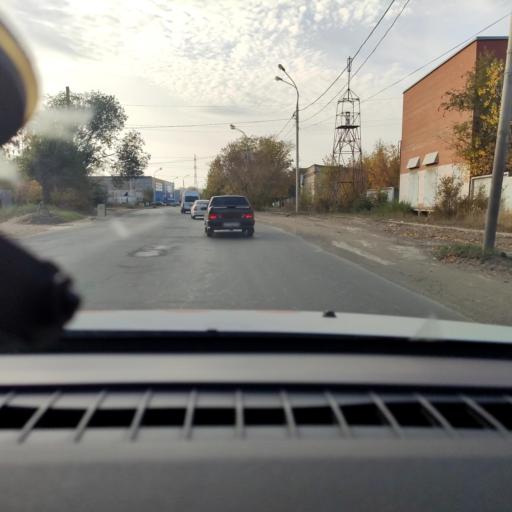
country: RU
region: Samara
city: Samara
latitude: 53.1340
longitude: 50.1216
